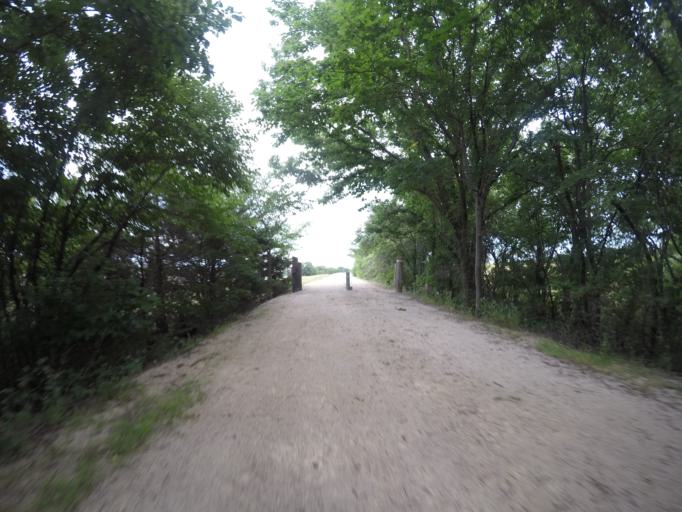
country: US
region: Kansas
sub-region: Anderson County
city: Garnett
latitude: 38.3050
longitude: -95.2453
